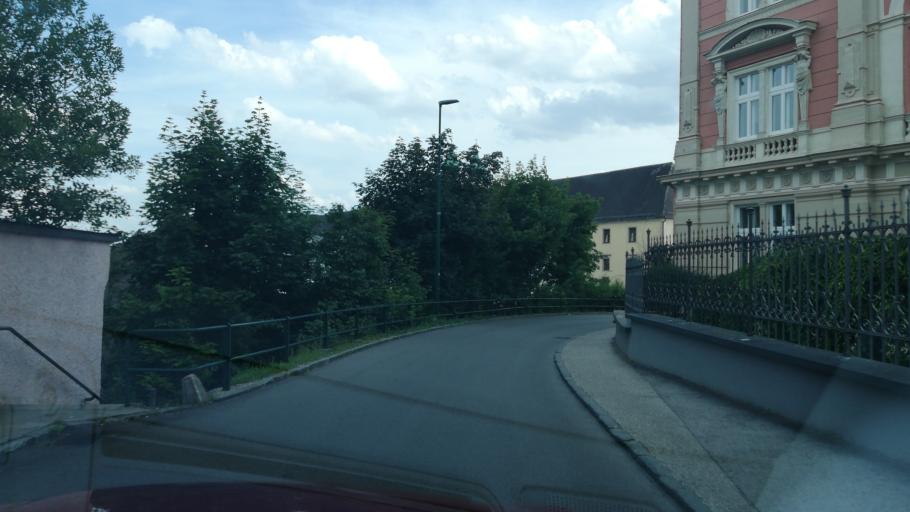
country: AT
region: Upper Austria
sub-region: Wels-Land
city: Lambach
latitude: 48.0921
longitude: 13.8749
